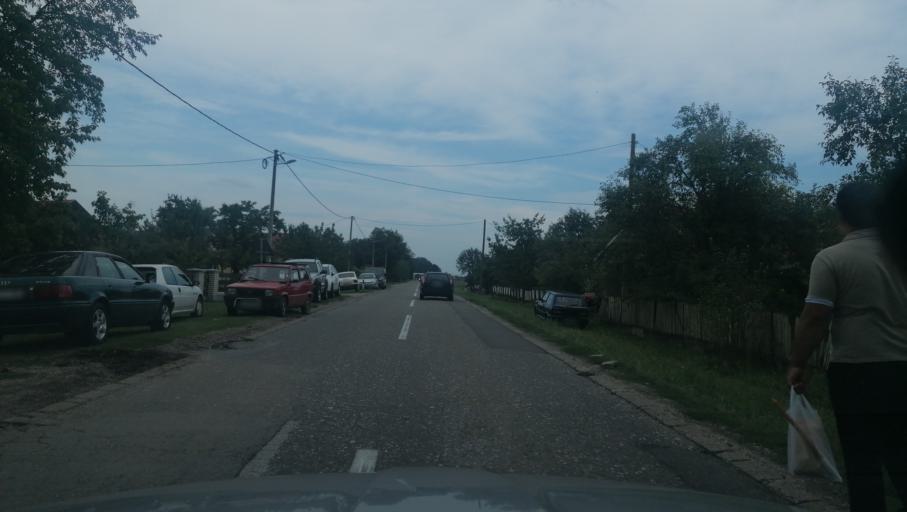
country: RS
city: Klenje
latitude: 44.8205
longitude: 19.4513
